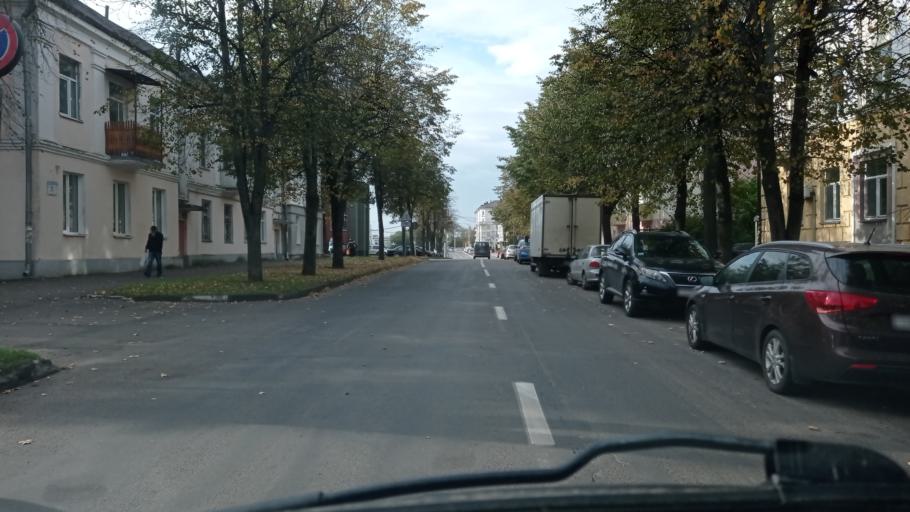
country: BY
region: Vitebsk
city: Vitebsk
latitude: 55.1839
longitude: 30.2086
